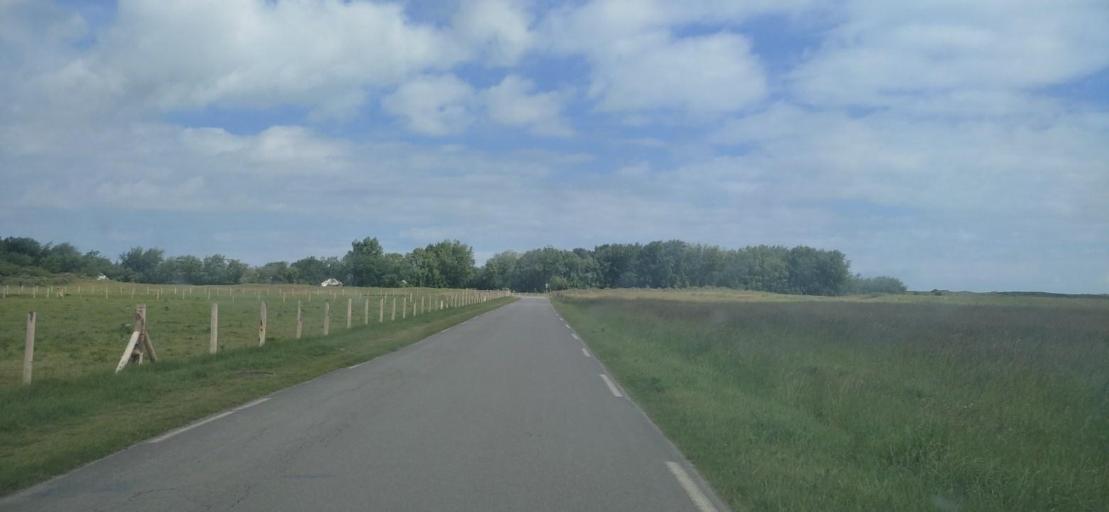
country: FR
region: Nord-Pas-de-Calais
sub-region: Departement du Pas-de-Calais
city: Oye-Plage
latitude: 51.0005
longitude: 2.0687
